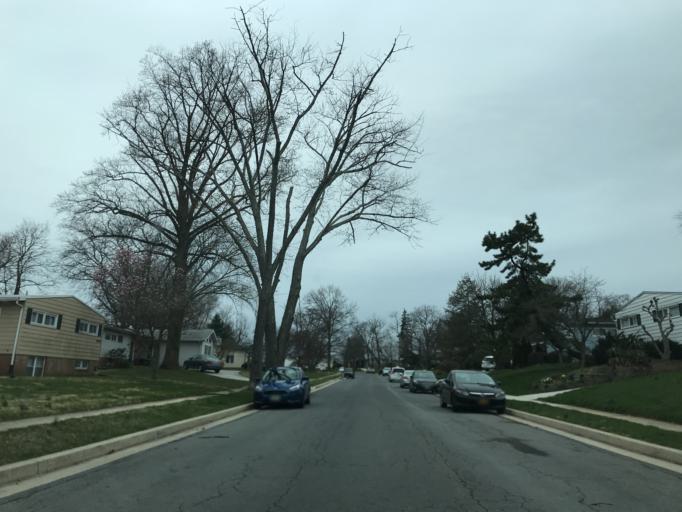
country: US
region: Maryland
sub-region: Baltimore County
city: Pikesville
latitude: 39.3787
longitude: -76.6784
